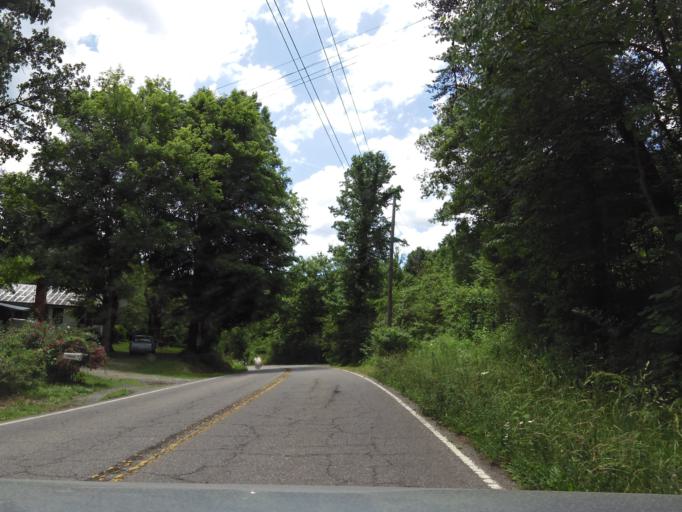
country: US
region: Tennessee
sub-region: Loudon County
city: Greenback
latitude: 35.5726
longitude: -84.0946
